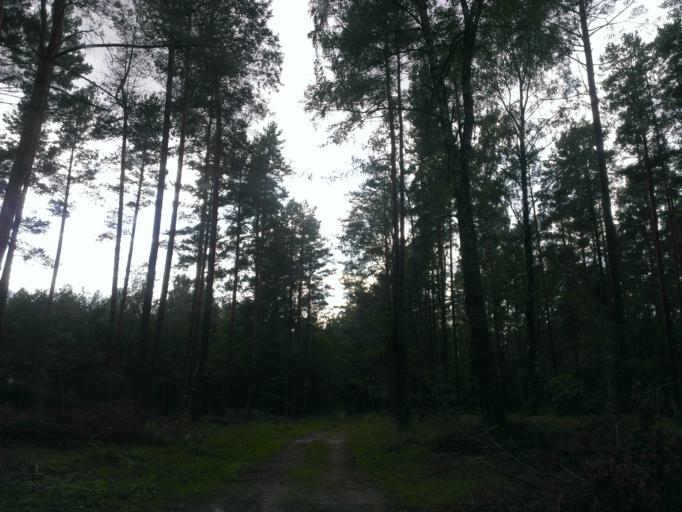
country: LV
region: Incukalns
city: Vangazi
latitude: 57.1067
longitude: 24.5323
